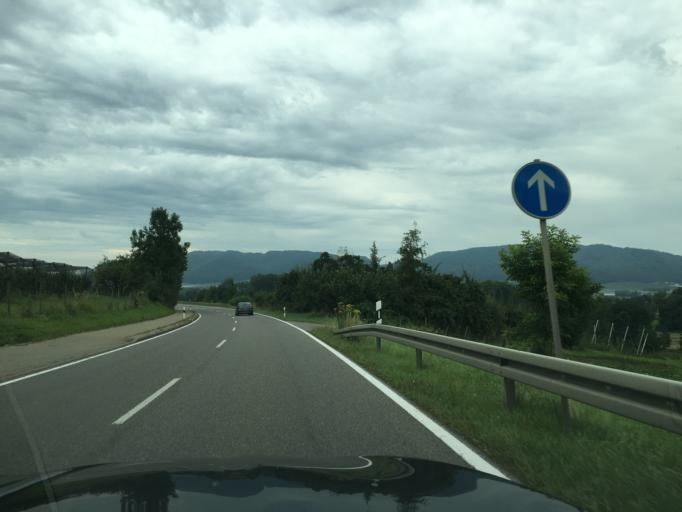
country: DE
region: Baden-Wuerttemberg
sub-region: Freiburg Region
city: Stockach
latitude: 47.8268
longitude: 8.9972
